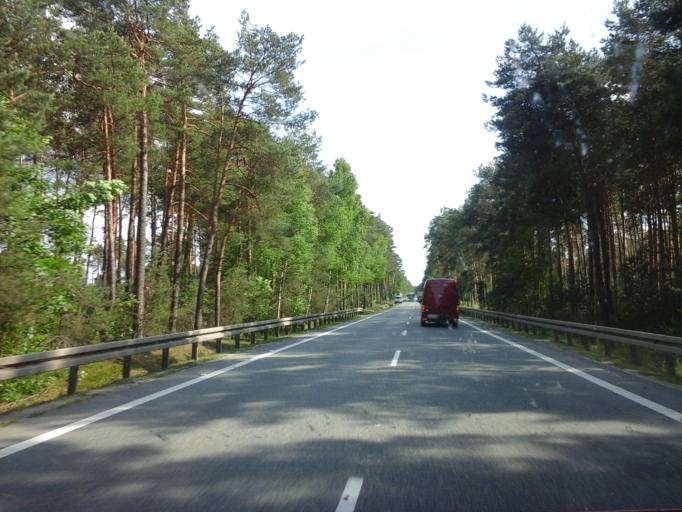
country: PL
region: Swietokrzyskie
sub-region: Powiat konecki
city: Ruda Maleniecka
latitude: 51.1798
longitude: 20.2198
